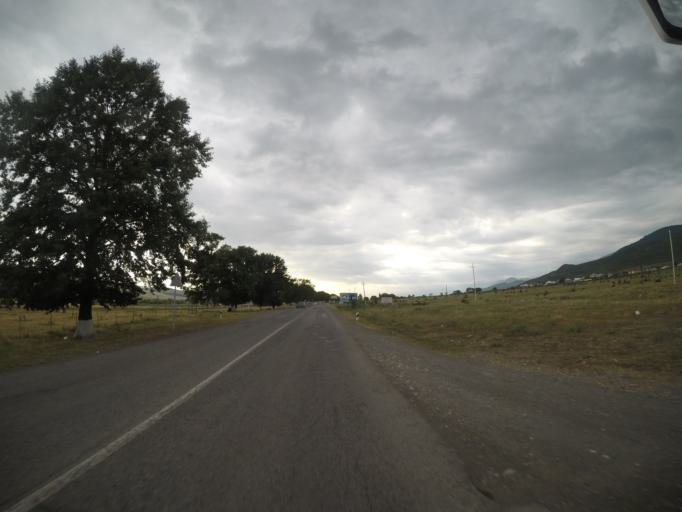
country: AZ
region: Ismayilli
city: Ismayilli
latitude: 40.7575
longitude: 48.2204
